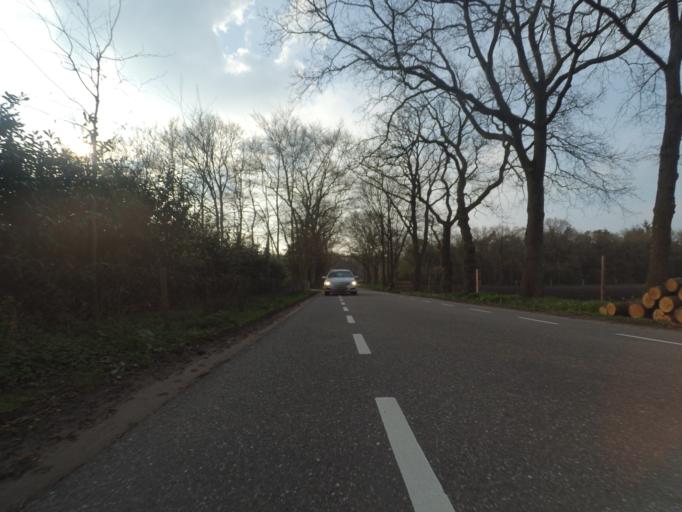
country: NL
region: Gelderland
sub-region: Gemeente Apeldoorn
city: Beekbergen
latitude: 52.1234
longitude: 5.8921
